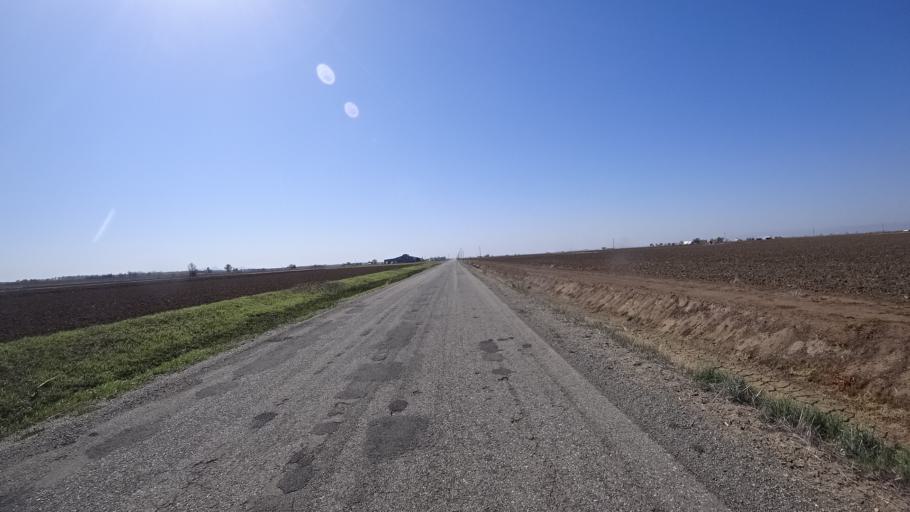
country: US
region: California
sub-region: Glenn County
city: Willows
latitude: 39.4454
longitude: -122.0317
